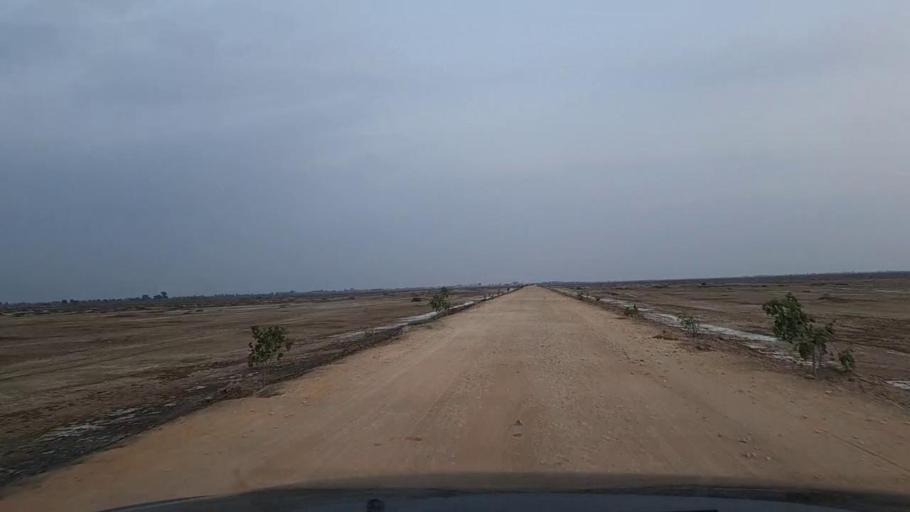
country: PK
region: Sindh
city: Jati
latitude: 24.5019
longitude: 68.3797
